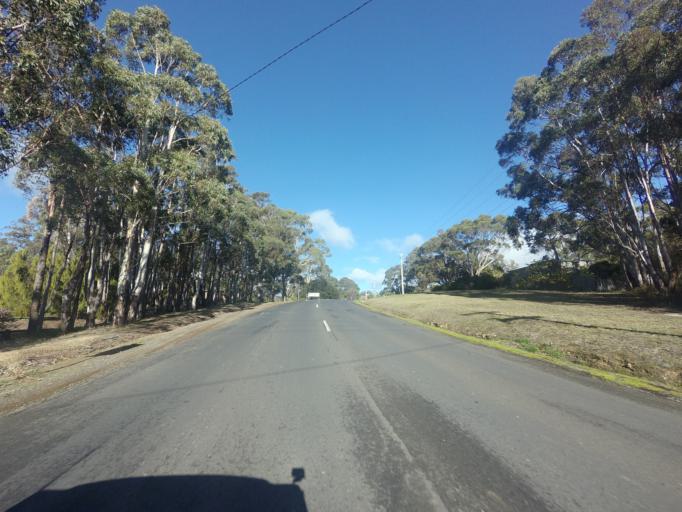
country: AU
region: Tasmania
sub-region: Glenorchy
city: Berriedale
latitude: -42.8237
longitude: 147.2039
